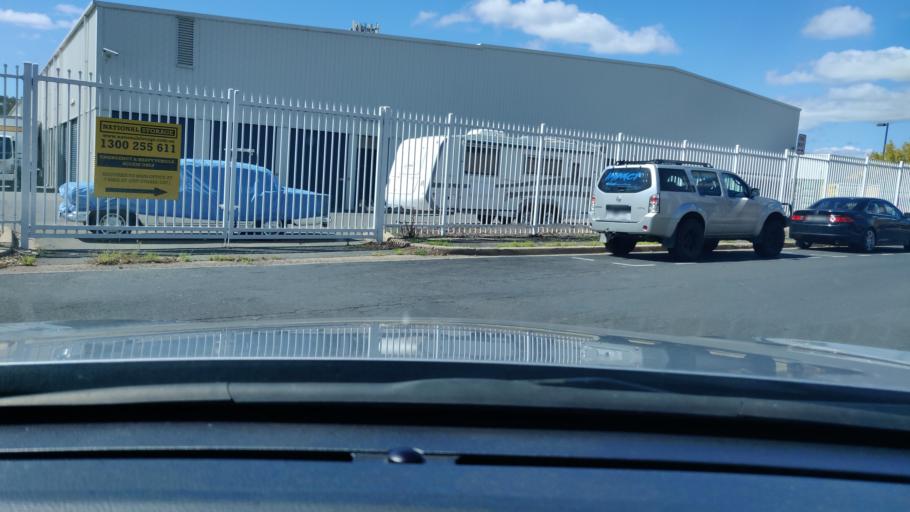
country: AU
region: Australian Capital Territory
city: Forrest
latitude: -35.3510
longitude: 149.0890
